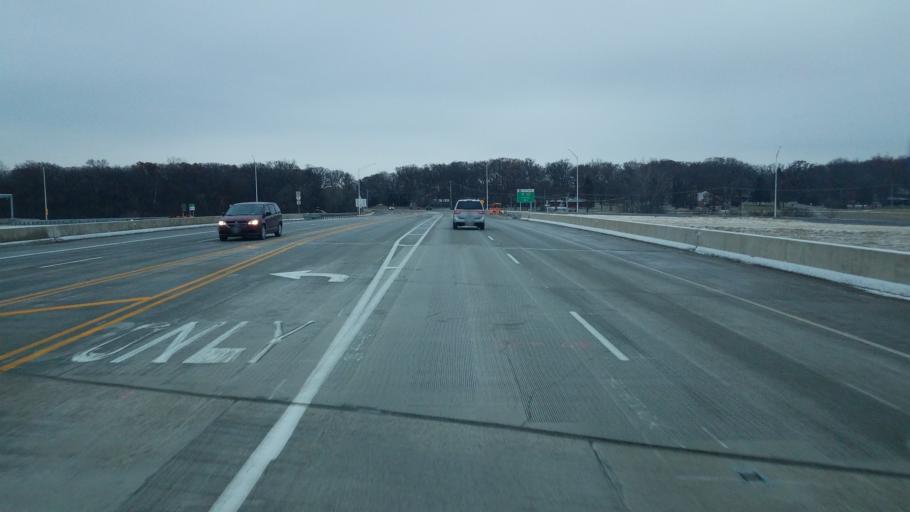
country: US
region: Illinois
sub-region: Kane County
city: Sugar Grove
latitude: 41.8190
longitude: -88.4666
